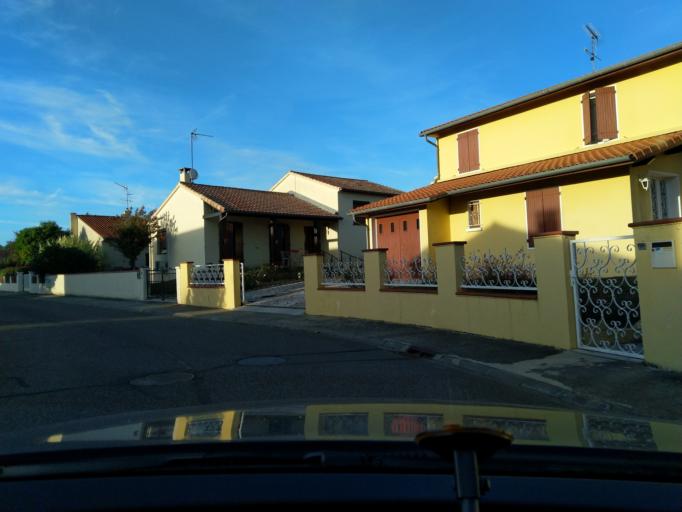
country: FR
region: Midi-Pyrenees
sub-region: Departement de la Haute-Garonne
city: Tournefeuille
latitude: 43.5758
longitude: 1.3298
